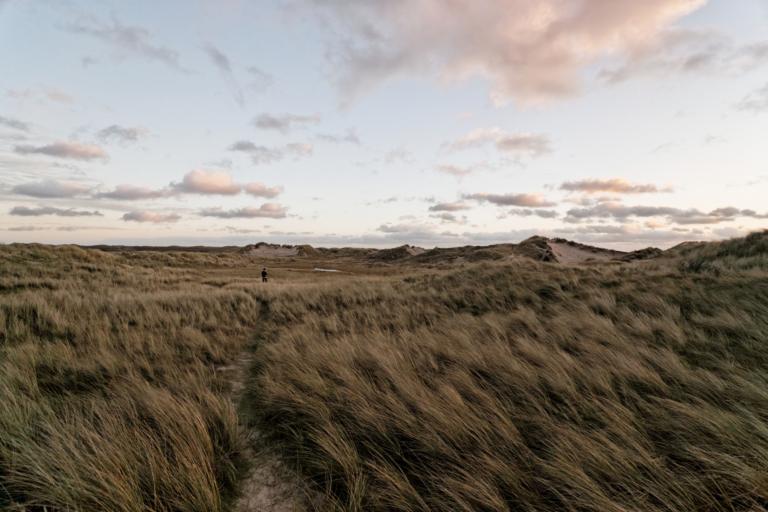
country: NL
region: North Holland
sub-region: Gemeente Texel
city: Den Burg
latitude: 53.1338
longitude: 4.8022
